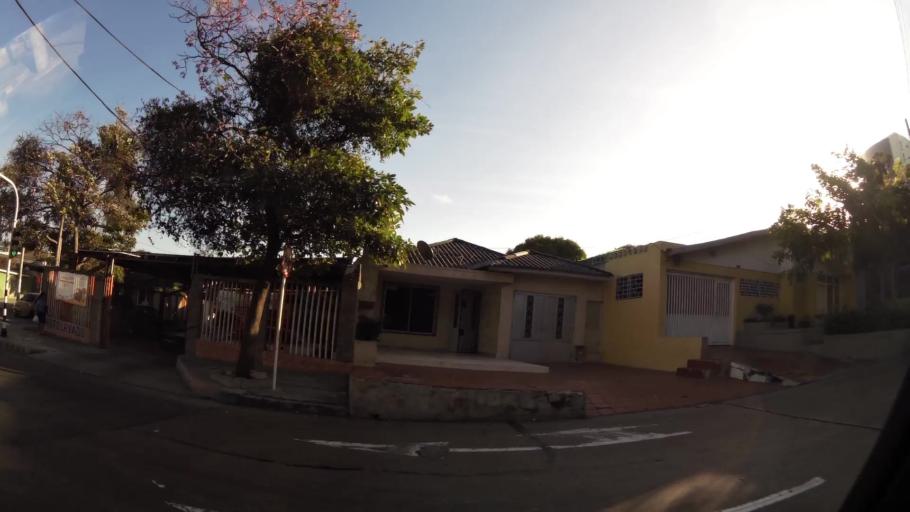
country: CO
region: Atlantico
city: Barranquilla
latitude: 10.9834
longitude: -74.8037
